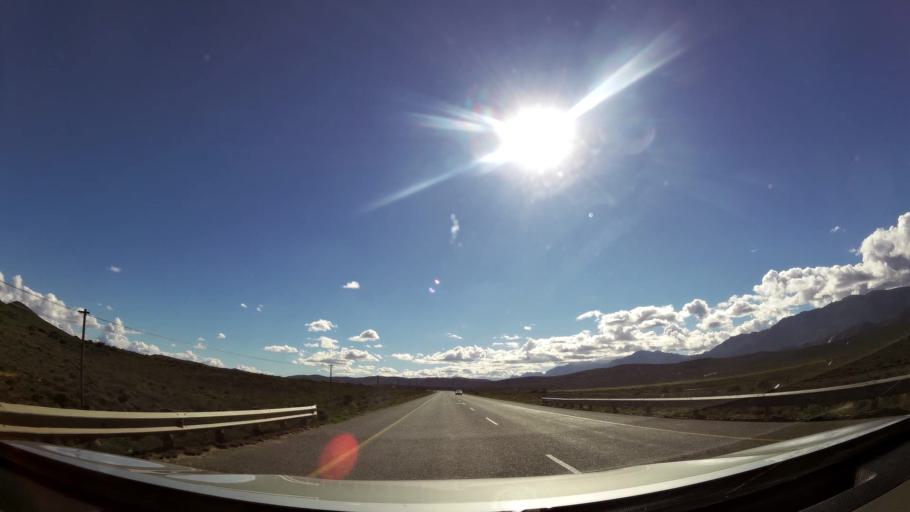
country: ZA
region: Western Cape
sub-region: Cape Winelands District Municipality
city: Worcester
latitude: -33.7559
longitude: 19.7312
